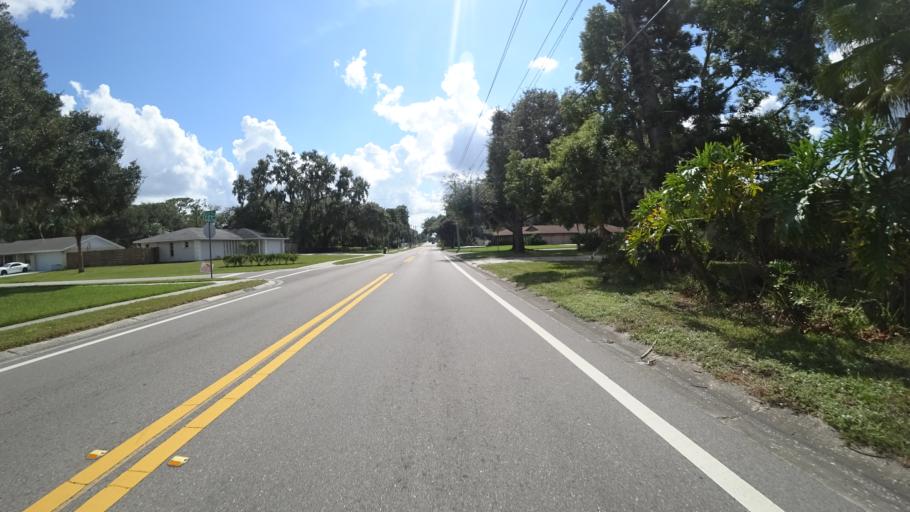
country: US
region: Florida
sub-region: Manatee County
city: Whitfield
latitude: 27.4208
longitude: -82.5550
